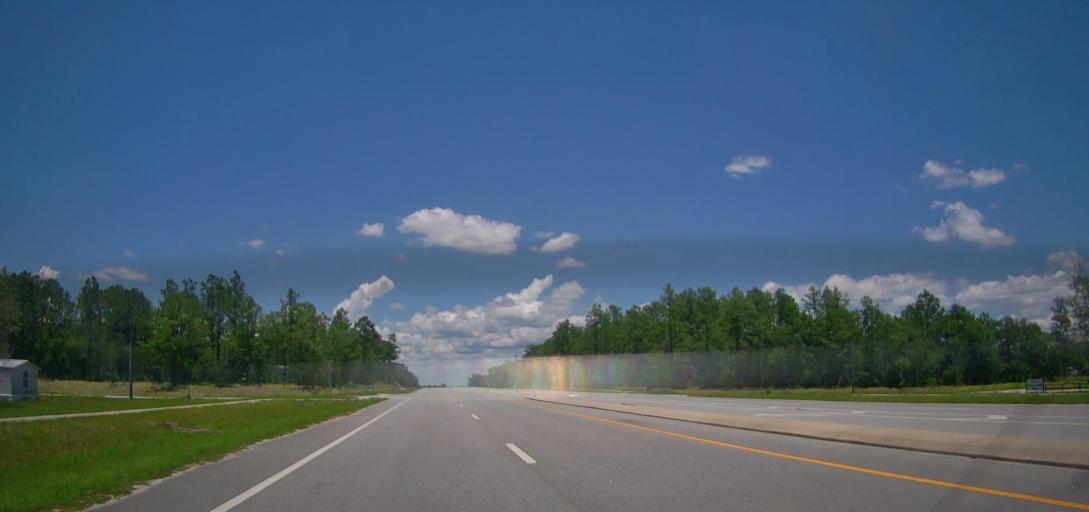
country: US
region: Florida
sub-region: Marion County
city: Belleview
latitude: 29.0417
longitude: -82.0176
